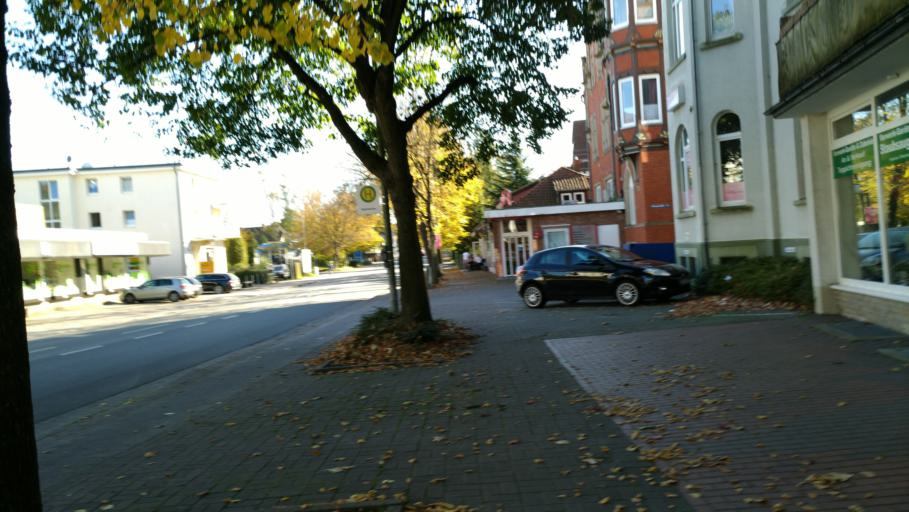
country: DE
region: Lower Saxony
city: Rinteln
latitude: 52.1954
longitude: 9.0799
